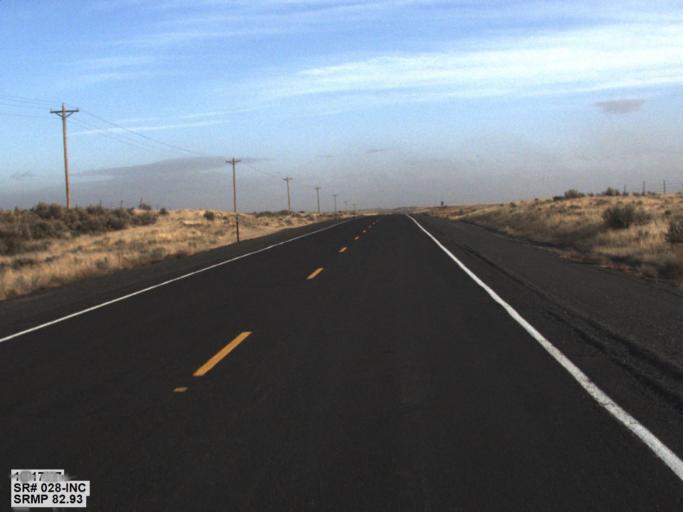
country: US
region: Washington
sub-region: Grant County
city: Warden
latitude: 47.3398
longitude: -118.9056
